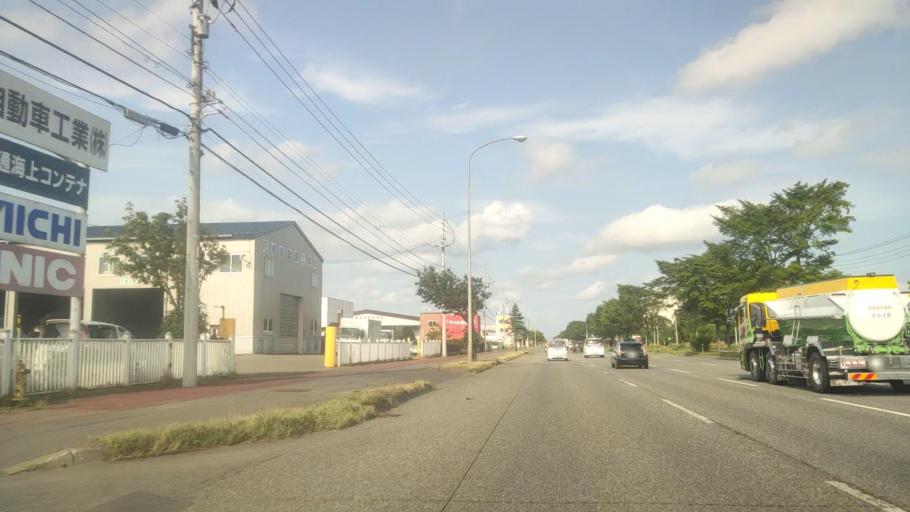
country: JP
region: Hokkaido
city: Tomakomai
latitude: 42.6562
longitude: 141.6543
